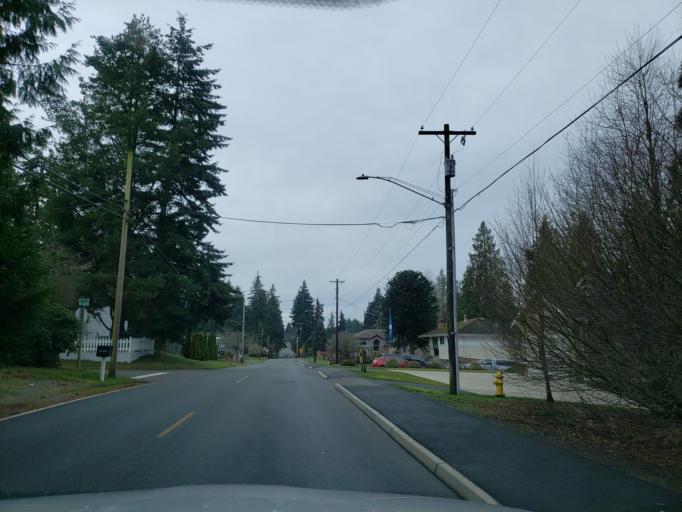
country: US
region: Washington
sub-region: Snohomish County
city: Lynnwood
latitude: 47.8260
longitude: -122.3413
